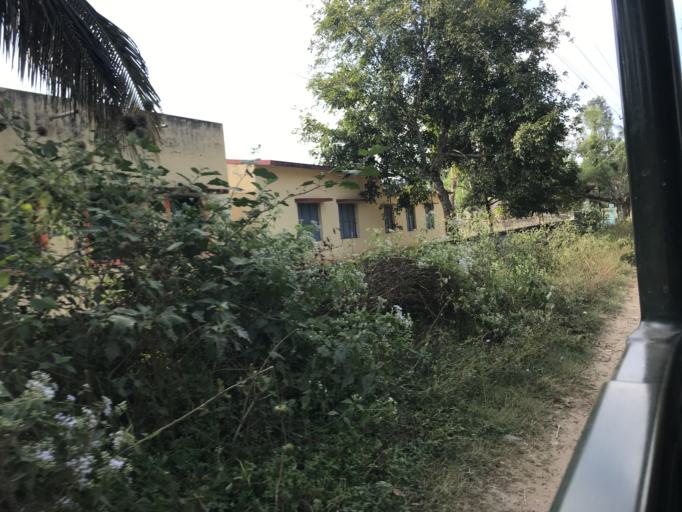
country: IN
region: Karnataka
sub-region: Mysore
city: Heggadadevankote
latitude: 11.9471
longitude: 76.2556
